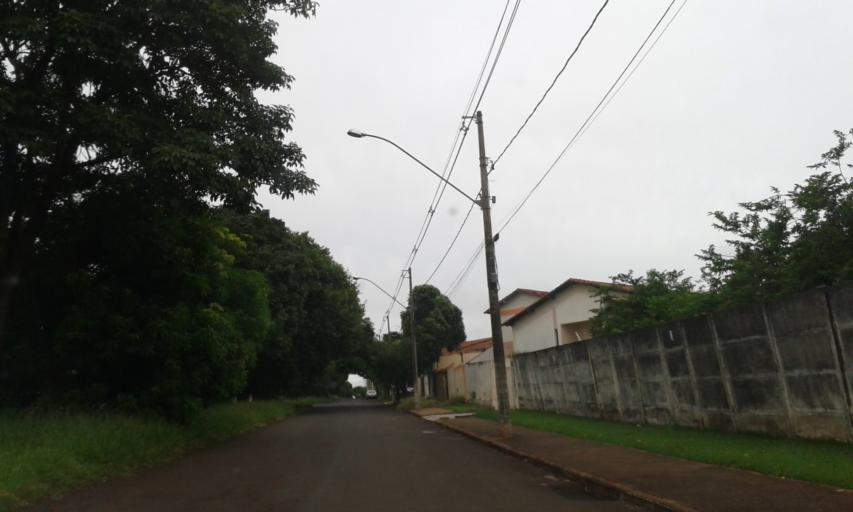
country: BR
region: Minas Gerais
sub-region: Ituiutaba
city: Ituiutaba
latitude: -18.9716
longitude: -49.4513
